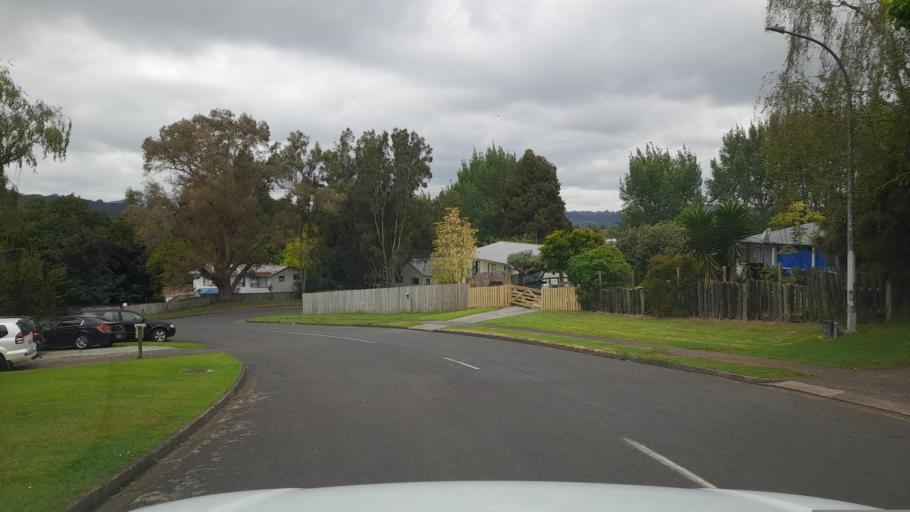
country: NZ
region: Northland
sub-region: Far North District
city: Waimate North
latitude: -35.4044
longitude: 173.7853
